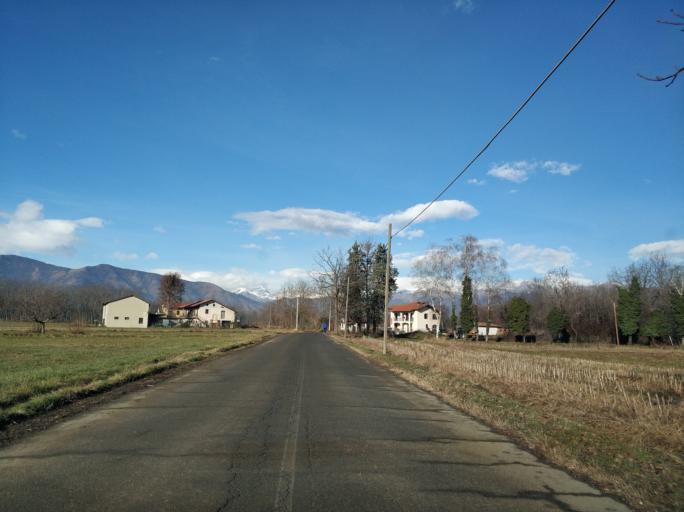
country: IT
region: Piedmont
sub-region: Provincia di Torino
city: Cirie
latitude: 45.2205
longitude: 7.5785
